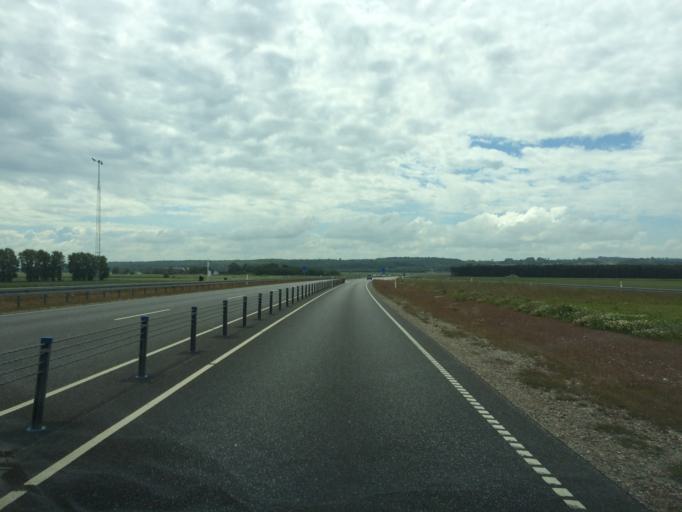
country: DK
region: Zealand
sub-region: Odsherred Kommune
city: Hojby
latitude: 55.8473
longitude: 11.6015
